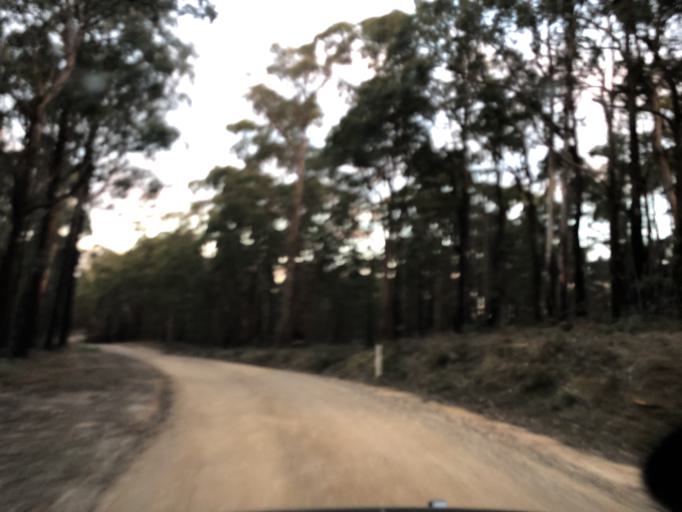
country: AU
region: Victoria
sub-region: Moorabool
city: Bacchus Marsh
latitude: -37.4715
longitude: 144.4195
